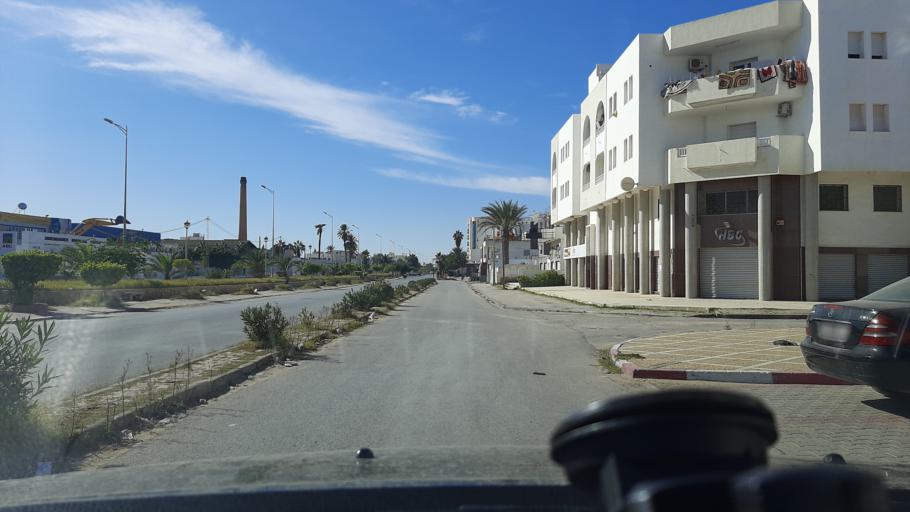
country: TN
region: Safaqis
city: Sfax
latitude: 34.7265
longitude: 10.7411
